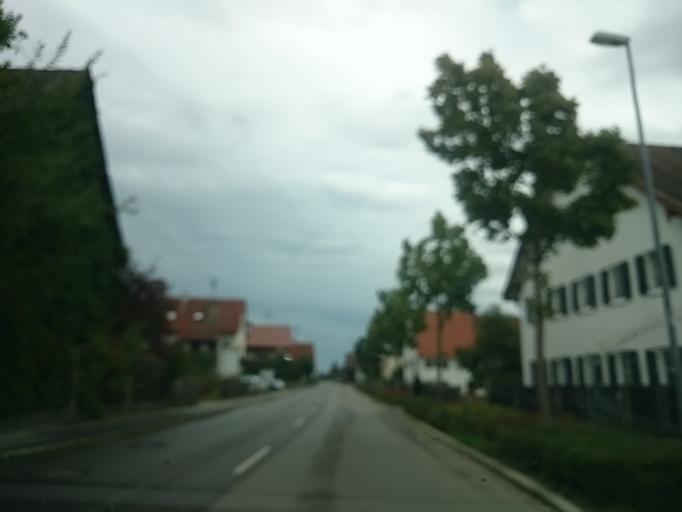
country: DE
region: Bavaria
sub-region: Swabia
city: Untermeitingen
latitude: 48.1629
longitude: 10.8079
